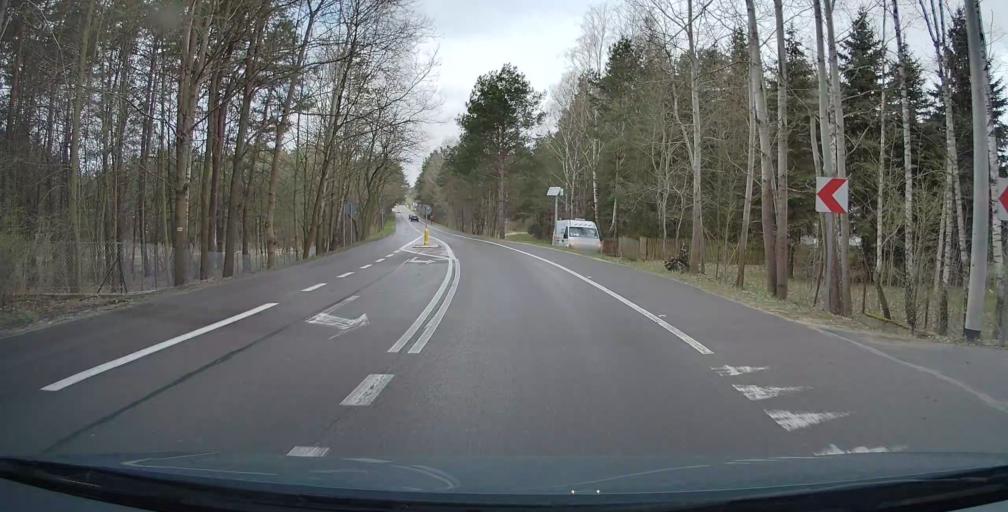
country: PL
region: Masovian Voivodeship
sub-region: Powiat wyszkowski
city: Dlugosiodlo
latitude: 52.7693
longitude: 21.5586
